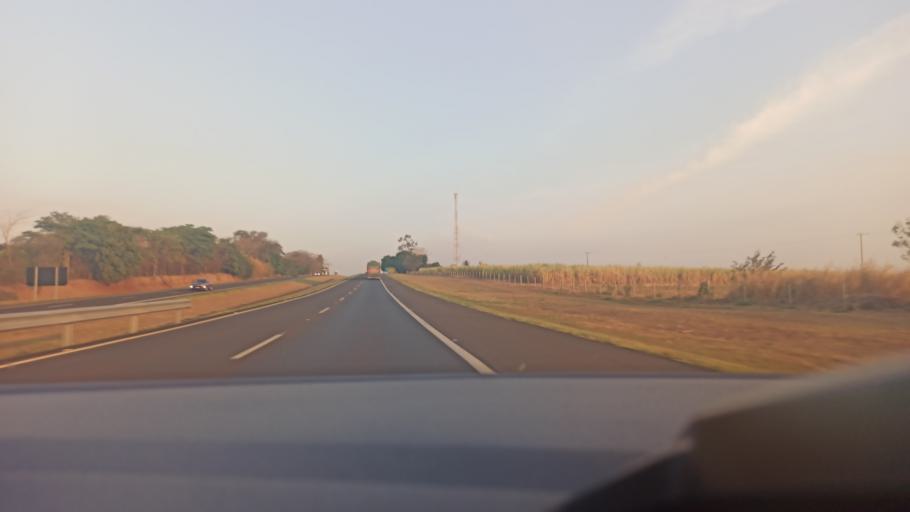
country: BR
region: Sao Paulo
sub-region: Taquaritinga
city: Taquaritinga
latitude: -21.4109
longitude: -48.6922
